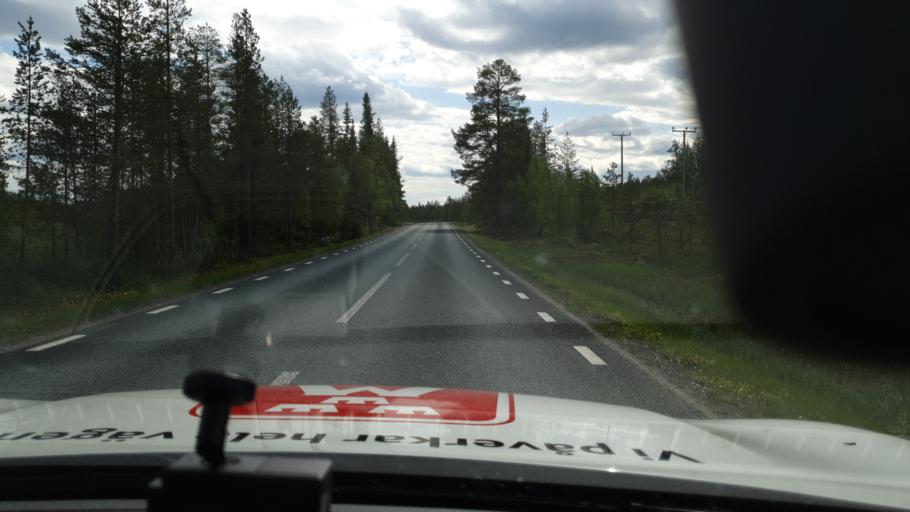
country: SE
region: Vaesterbotten
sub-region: Sorsele Kommun
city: Sorsele
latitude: 65.4191
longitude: 17.5671
